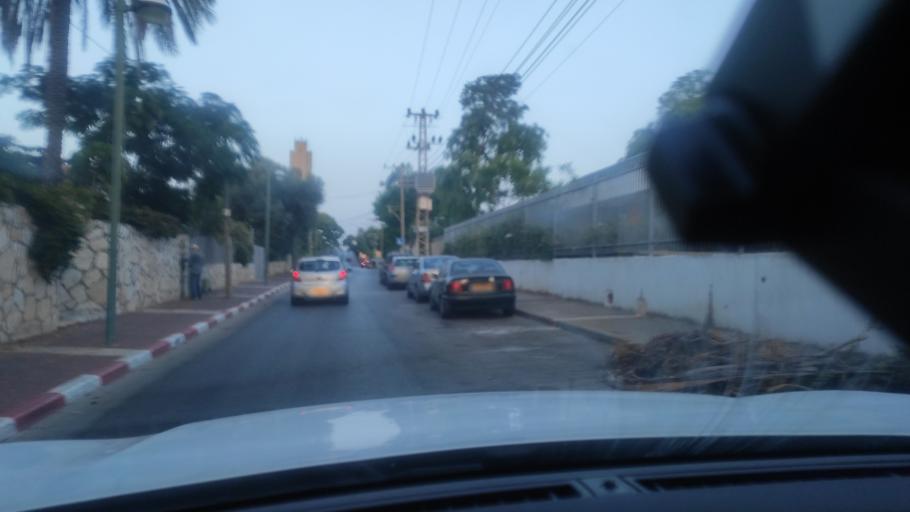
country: IL
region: Central District
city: Kfar Saba
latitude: 32.1847
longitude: 34.9060
